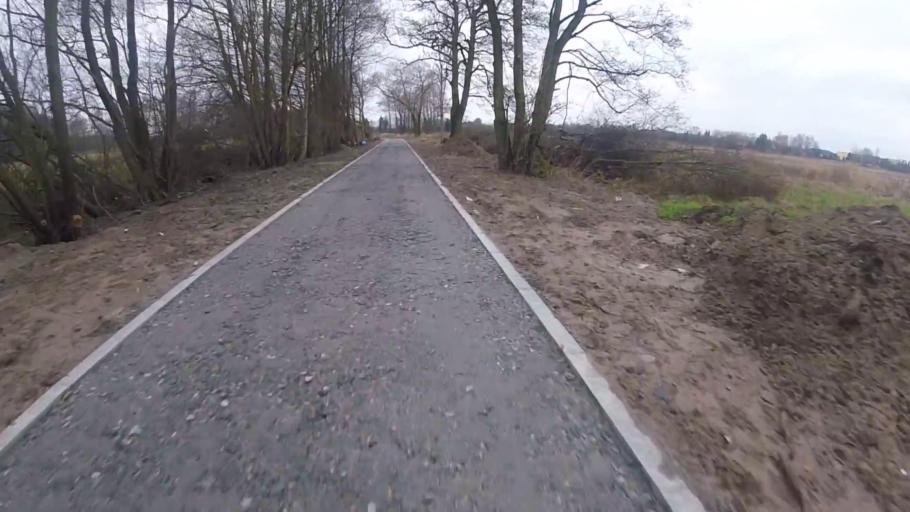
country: PL
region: West Pomeranian Voivodeship
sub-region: Koszalin
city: Koszalin
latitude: 54.2305
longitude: 16.1502
